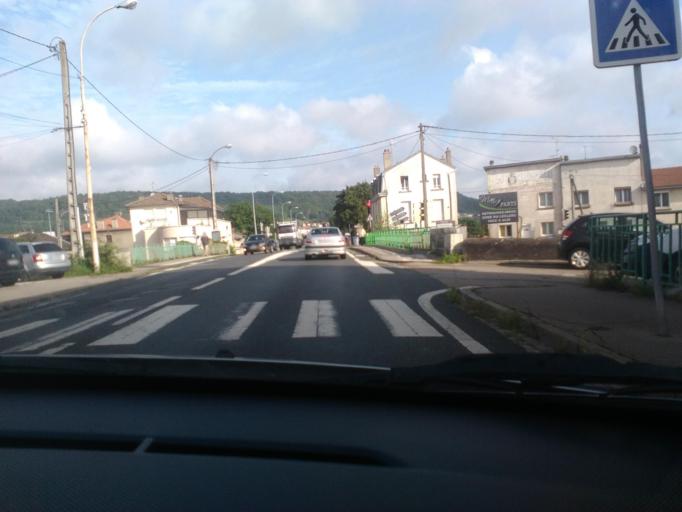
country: FR
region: Lorraine
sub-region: Departement de Meurthe-et-Moselle
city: Frouard
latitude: 48.7613
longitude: 6.1322
